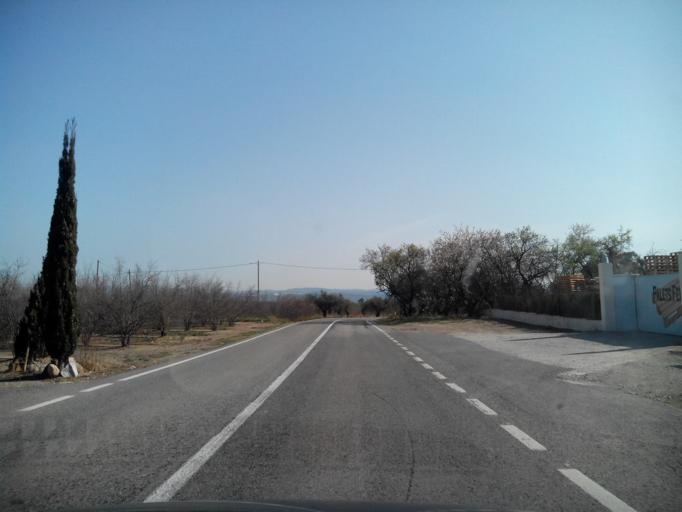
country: ES
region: Catalonia
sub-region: Provincia de Tarragona
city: La Selva
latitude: 41.2145
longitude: 1.1550
